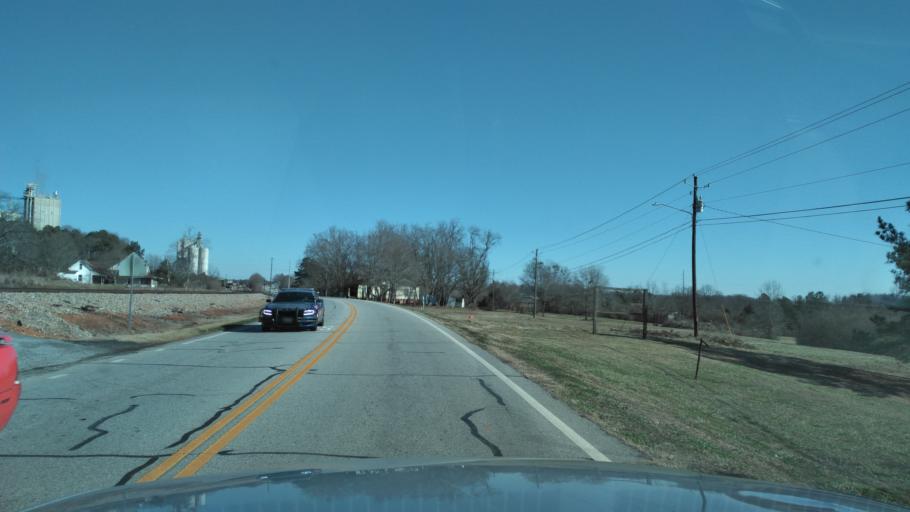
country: US
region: Georgia
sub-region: Banks County
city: Maysville
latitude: 34.2452
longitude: -83.5543
